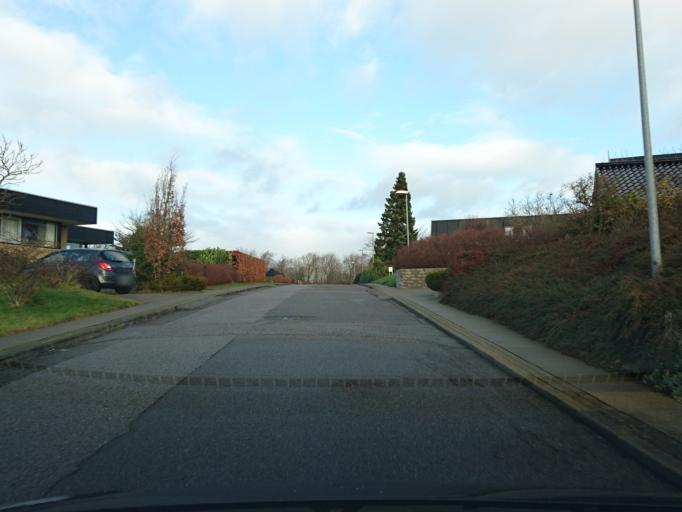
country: DK
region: North Denmark
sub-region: Alborg Kommune
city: Aalborg
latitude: 57.0159
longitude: 9.9410
